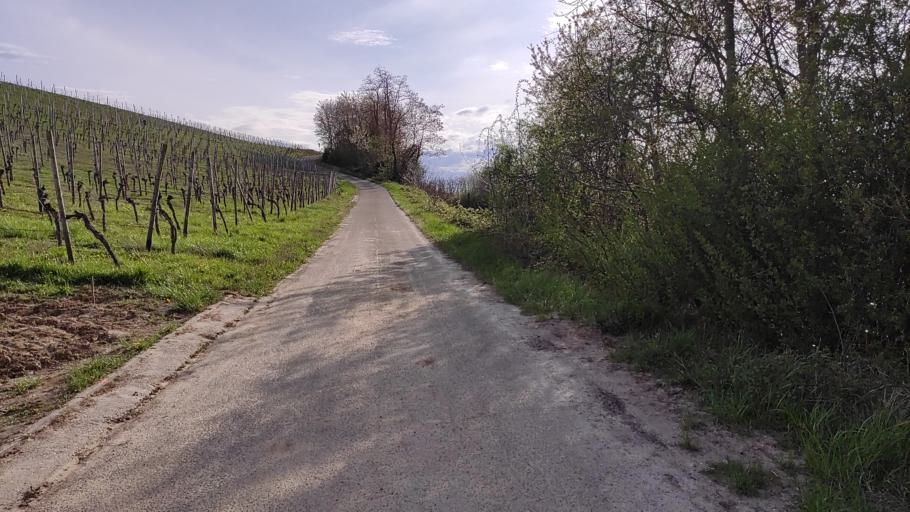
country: DE
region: Baden-Wuerttemberg
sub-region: Freiburg Region
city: Ebringen
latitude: 47.9654
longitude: 7.7750
